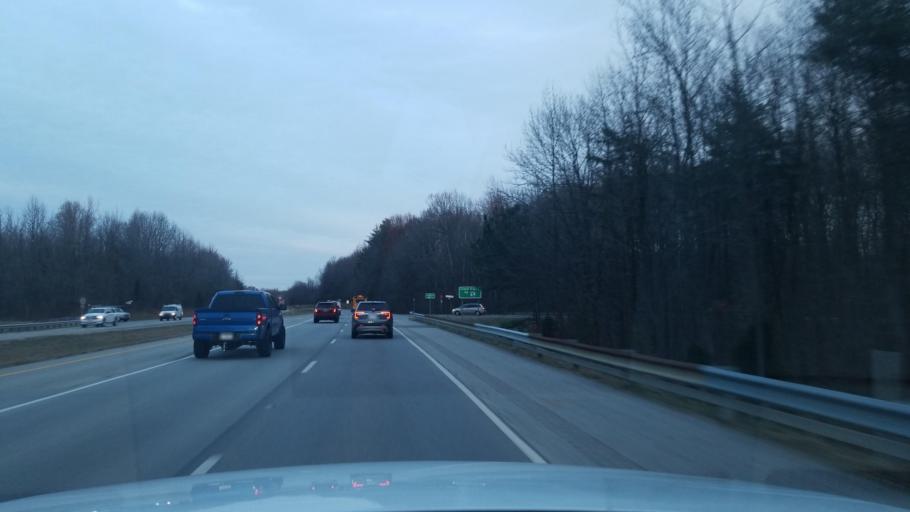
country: US
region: Indiana
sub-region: Vanderburgh County
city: Evansville
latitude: 37.9507
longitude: -87.7002
